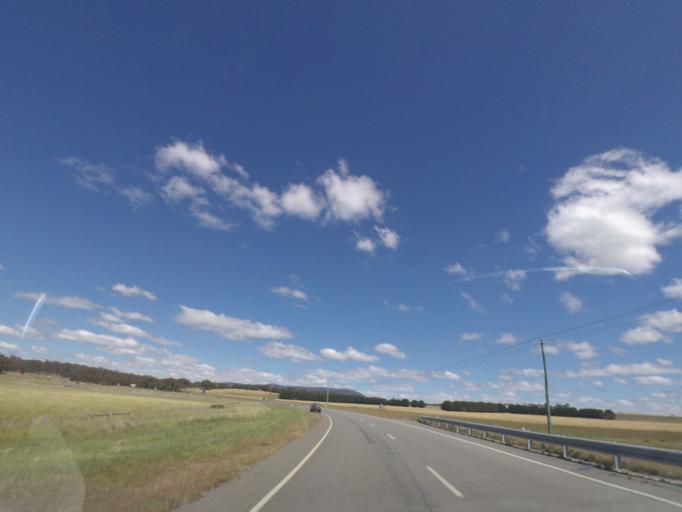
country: AU
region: Victoria
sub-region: Hume
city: Sunbury
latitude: -37.2952
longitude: 144.4989
